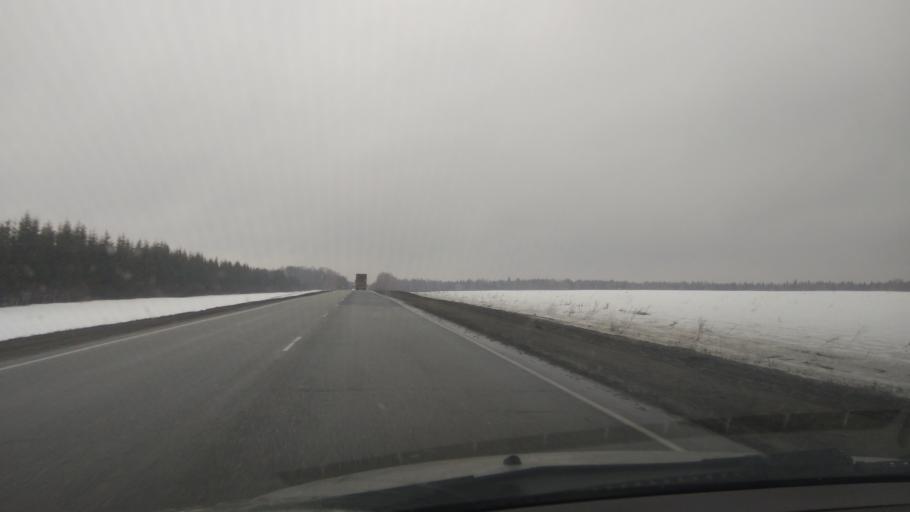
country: RU
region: Perm
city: Kukushtan
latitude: 57.5388
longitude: 56.6005
